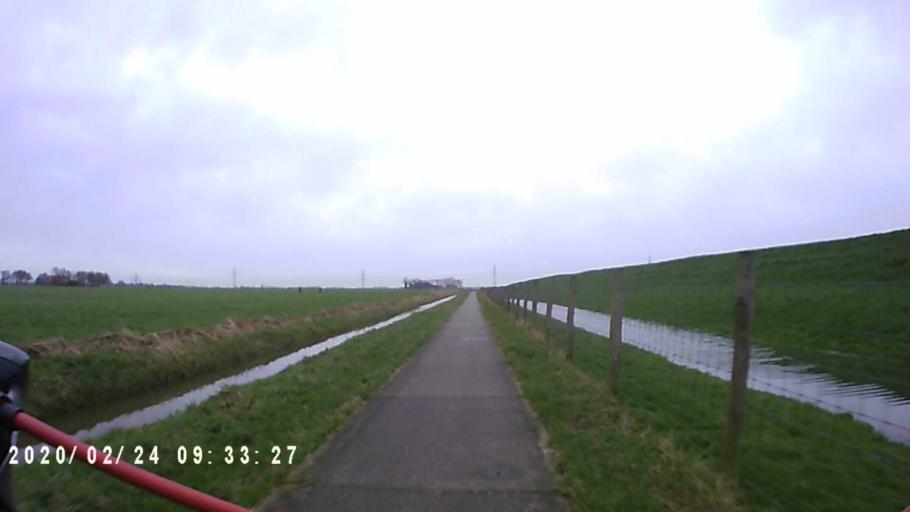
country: NL
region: Groningen
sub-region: Gemeente Winsum
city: Winsum
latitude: 53.3016
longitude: 6.4996
